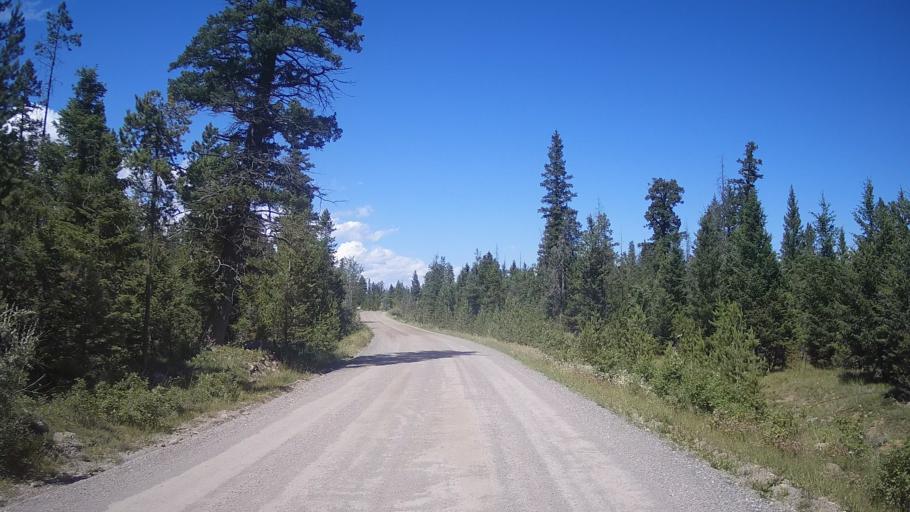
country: CA
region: British Columbia
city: Cache Creek
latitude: 51.1692
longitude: -121.5654
